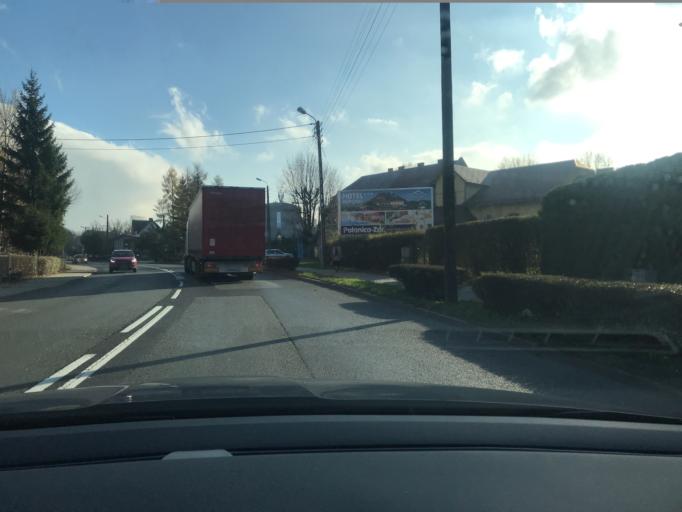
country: PL
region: Lower Silesian Voivodeship
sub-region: Powiat klodzki
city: Kudowa-Zdroj
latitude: 50.4326
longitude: 16.2407
